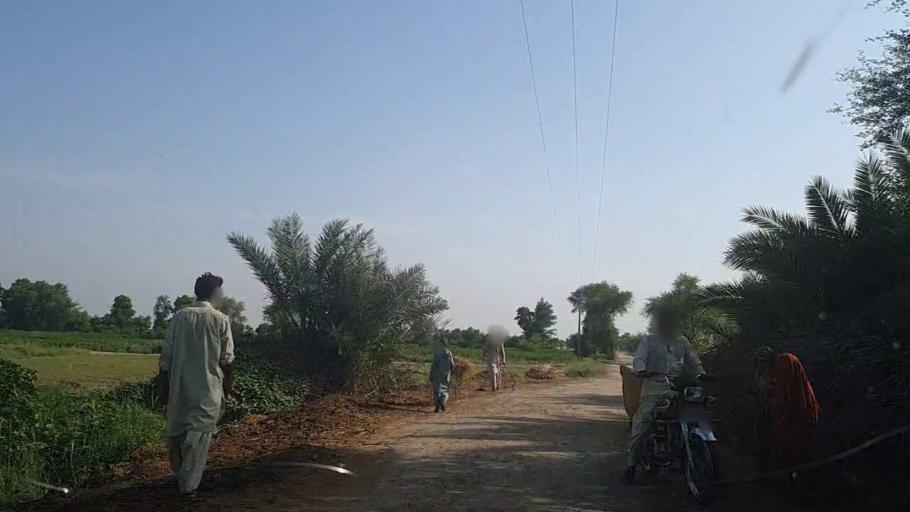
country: PK
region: Sindh
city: Khanpur
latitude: 27.7293
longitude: 69.3321
